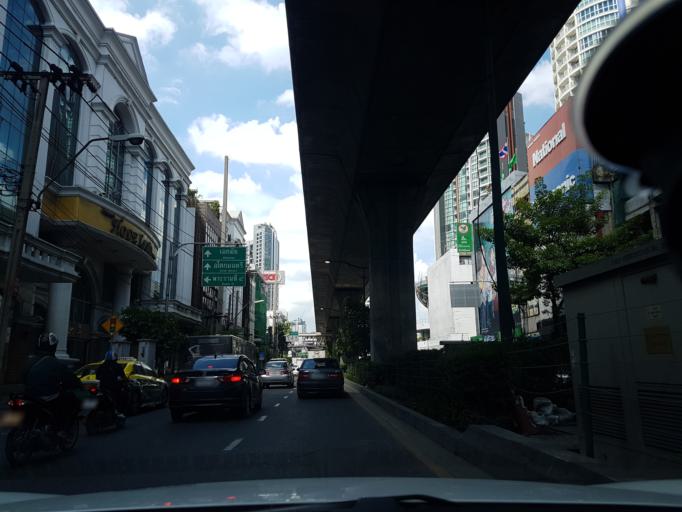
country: TH
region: Bangkok
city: Phra Khanong
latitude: 13.7132
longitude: 100.5940
